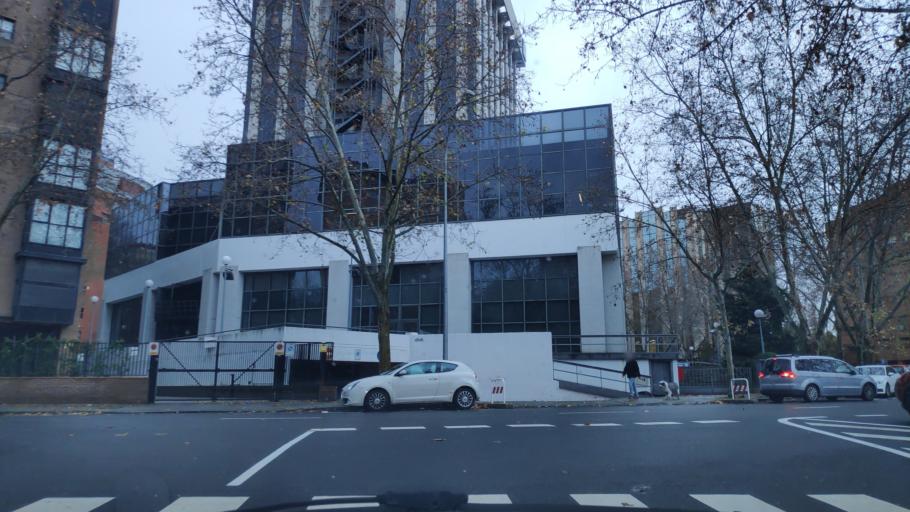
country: ES
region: Madrid
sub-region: Provincia de Madrid
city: Pinar de Chamartin
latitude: 40.4823
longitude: -3.6673
